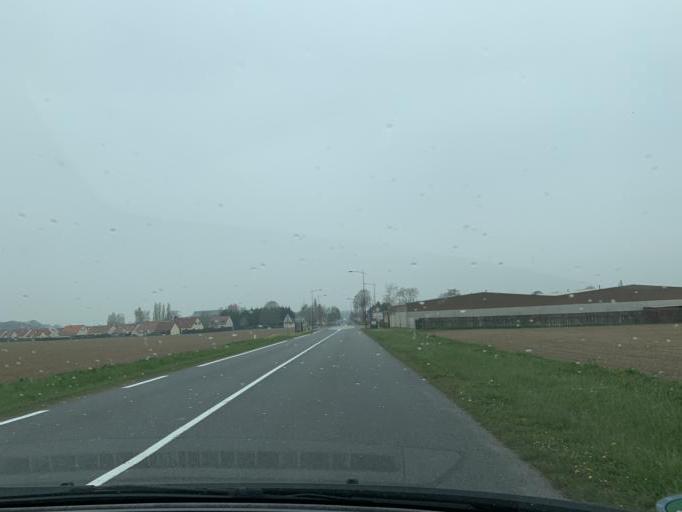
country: FR
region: Picardie
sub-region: Departement de la Somme
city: Nouvion
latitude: 50.1690
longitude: 1.8118
